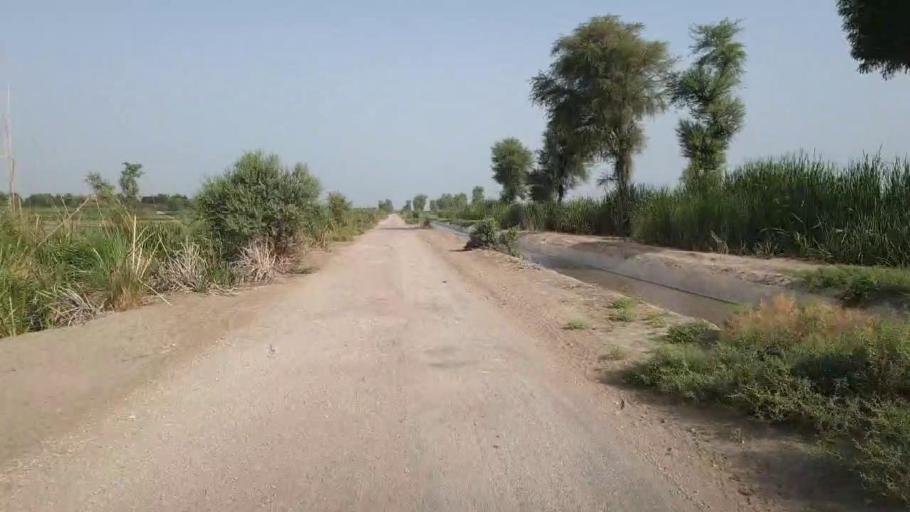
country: PK
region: Sindh
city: Daur
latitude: 26.3399
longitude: 68.1826
